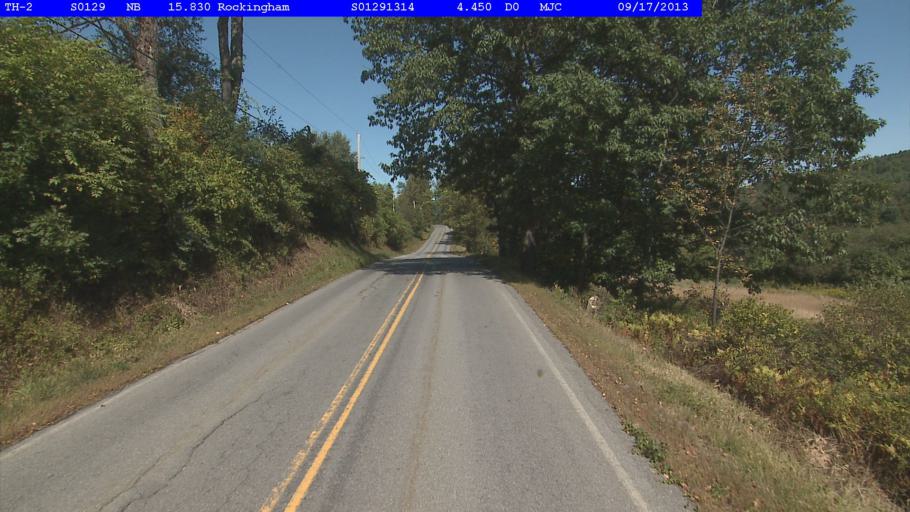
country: US
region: Vermont
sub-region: Windham County
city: Rockingham
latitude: 43.1810
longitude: -72.5149
